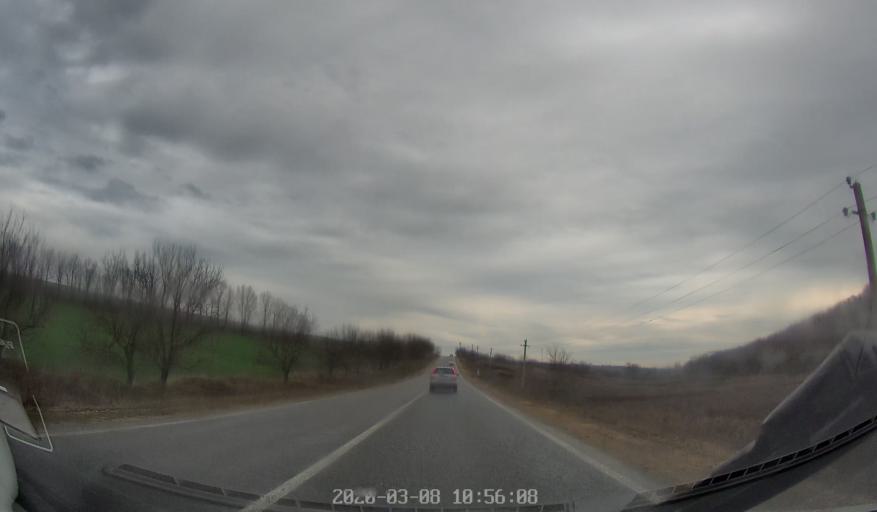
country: MD
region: Soldanesti
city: Soldanesti
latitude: 47.7002
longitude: 28.8359
